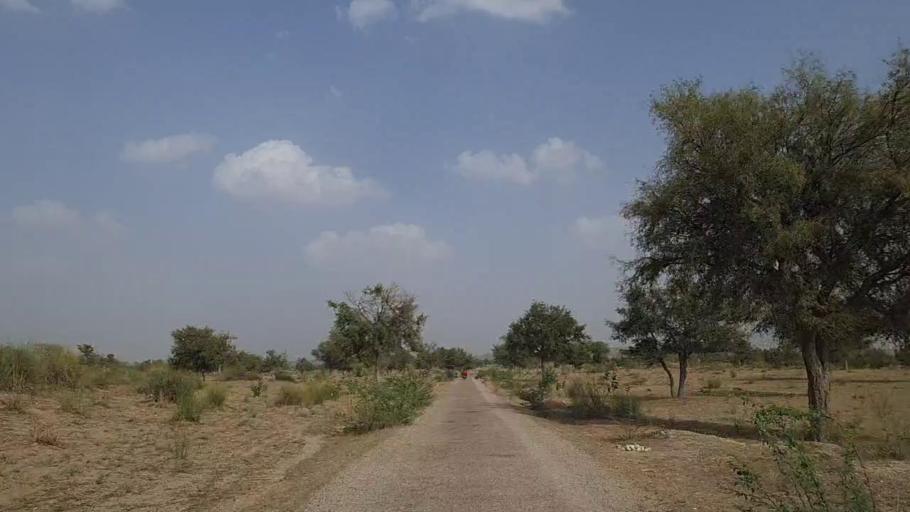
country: PK
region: Sindh
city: Islamkot
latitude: 24.8743
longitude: 70.1499
